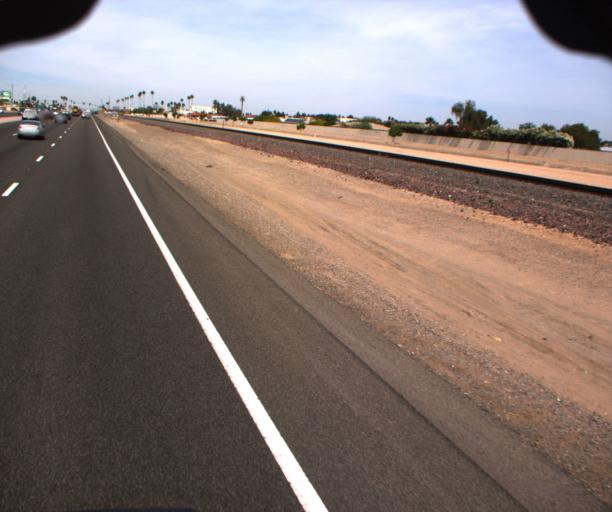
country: US
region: Arizona
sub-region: Maricopa County
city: Sun City
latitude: 33.5964
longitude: -112.2681
